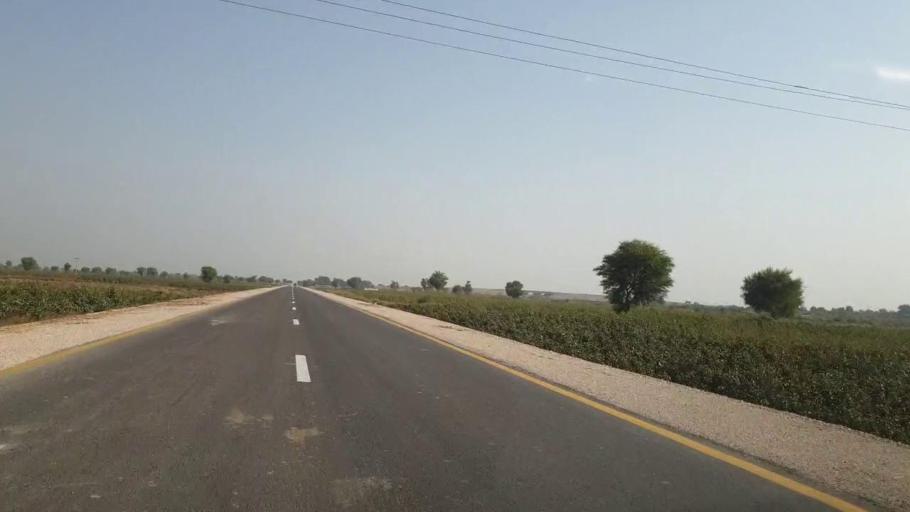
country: PK
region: Sindh
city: Sehwan
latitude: 26.4636
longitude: 67.7997
